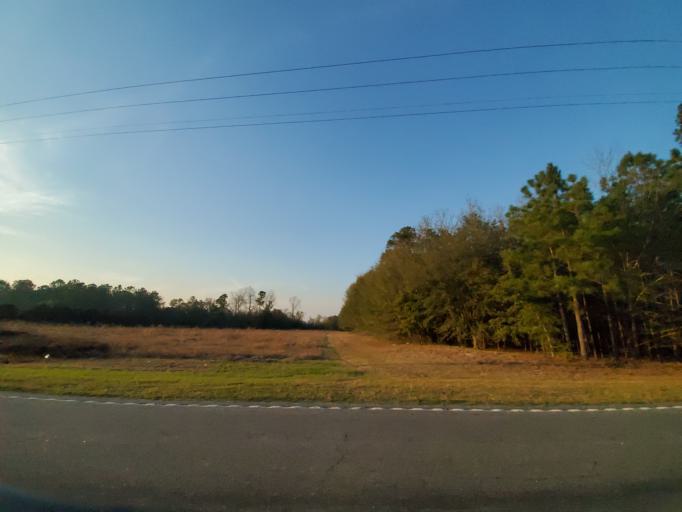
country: US
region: South Carolina
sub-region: Dorchester County
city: Saint George
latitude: 33.0481
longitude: -80.5251
